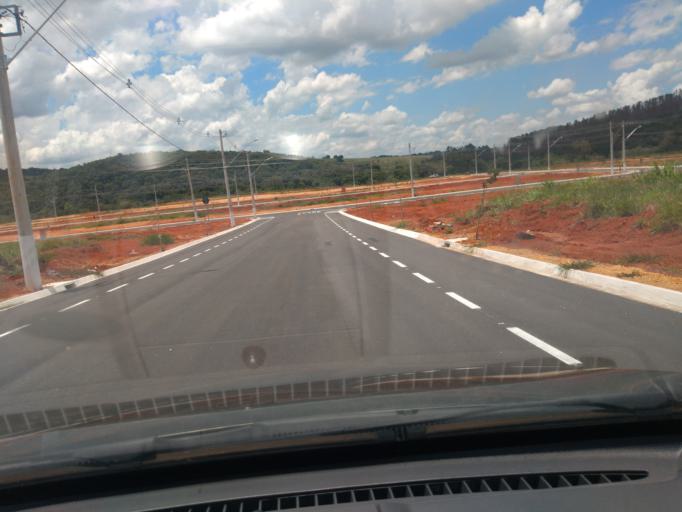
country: BR
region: Minas Gerais
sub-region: Tres Coracoes
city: Tres Coracoes
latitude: -21.6630
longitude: -45.2754
